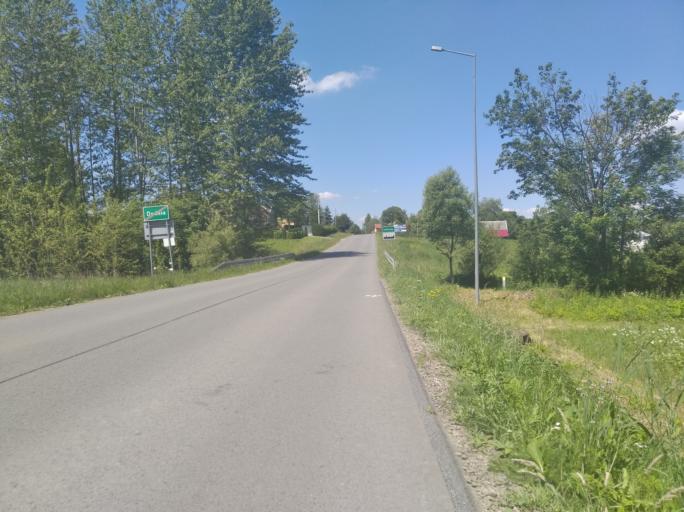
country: PL
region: Subcarpathian Voivodeship
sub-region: Powiat brzozowski
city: Jablonka
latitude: 49.6971
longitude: 22.1363
